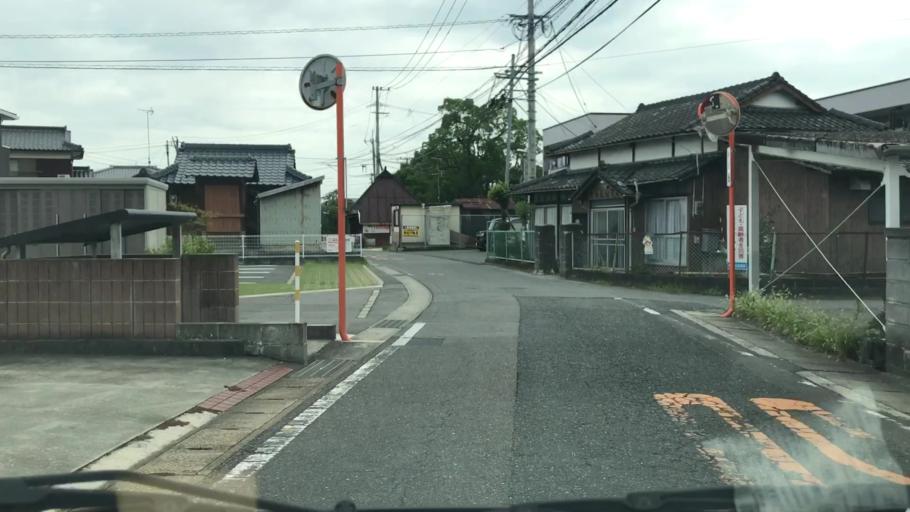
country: JP
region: Saga Prefecture
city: Saga-shi
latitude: 33.2712
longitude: 130.2631
